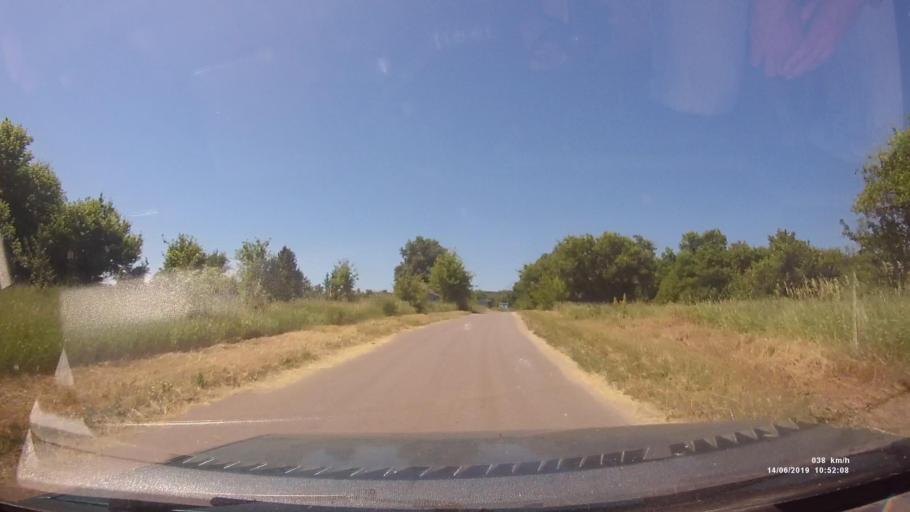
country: RU
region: Rostov
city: Kazanskaya
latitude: 49.8666
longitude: 41.3895
